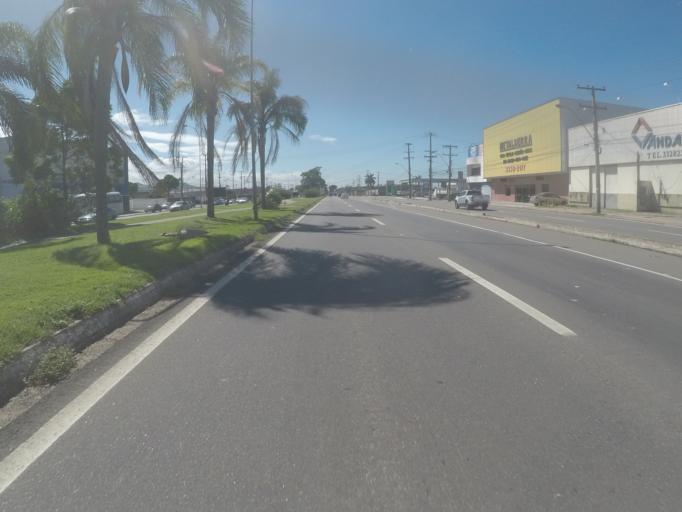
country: BR
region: Espirito Santo
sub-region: Serra
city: Serra
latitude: -20.2156
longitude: -40.2698
